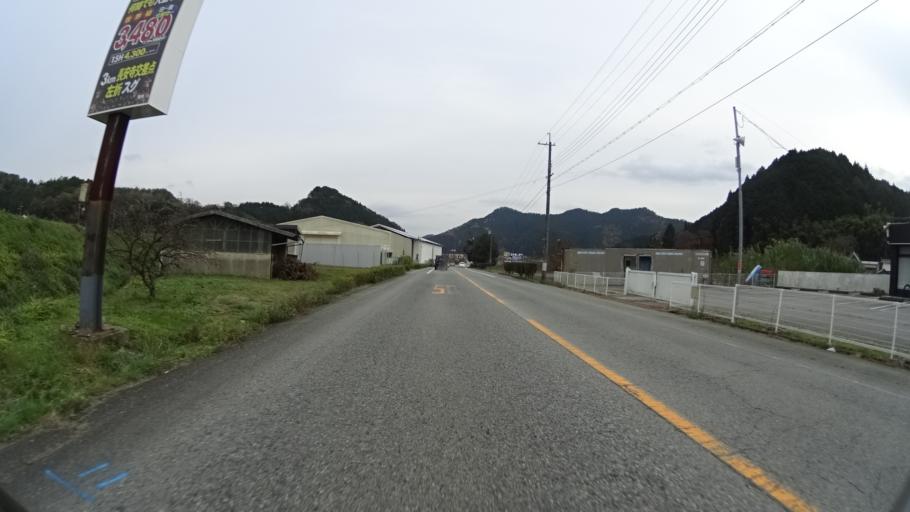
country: JP
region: Hyogo
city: Sasayama
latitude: 35.1026
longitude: 135.1299
